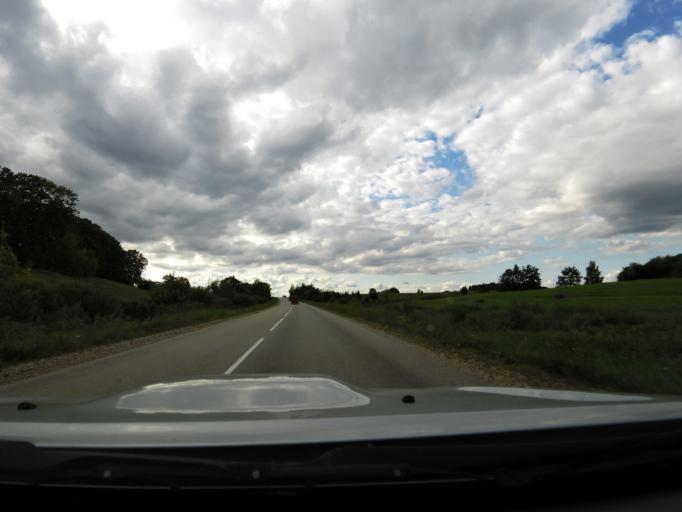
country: LV
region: Ilukste
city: Ilukste
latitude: 55.9784
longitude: 26.0099
